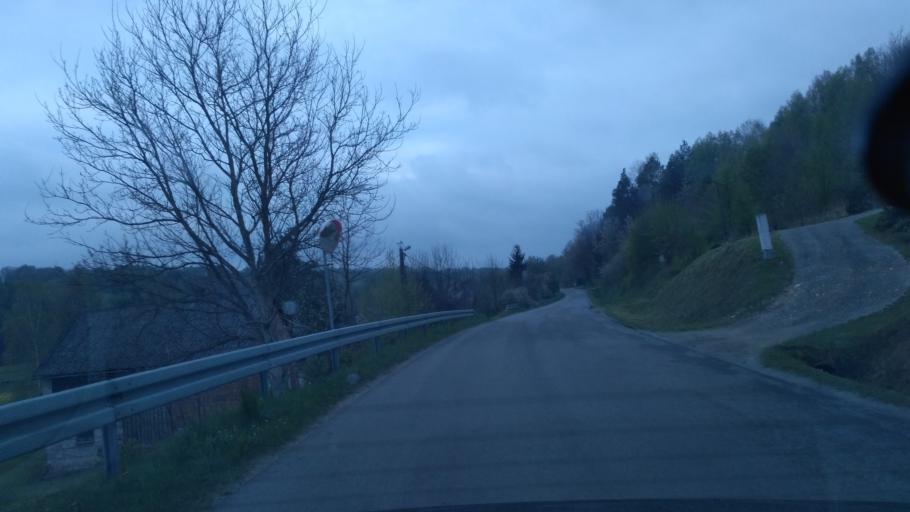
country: PL
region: Subcarpathian Voivodeship
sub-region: Powiat rzeszowski
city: Blazowa
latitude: 49.8730
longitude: 22.0644
